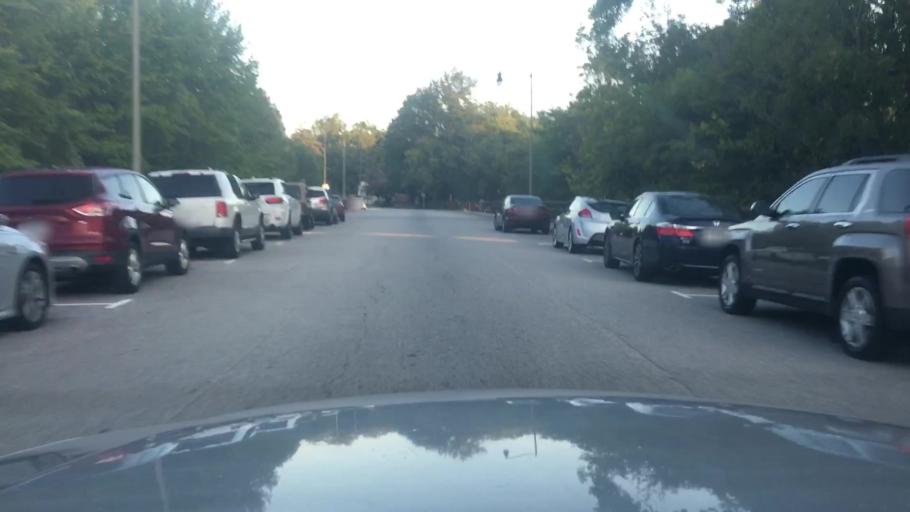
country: US
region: North Carolina
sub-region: Cumberland County
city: Fayetteville
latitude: 35.0540
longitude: -78.8784
